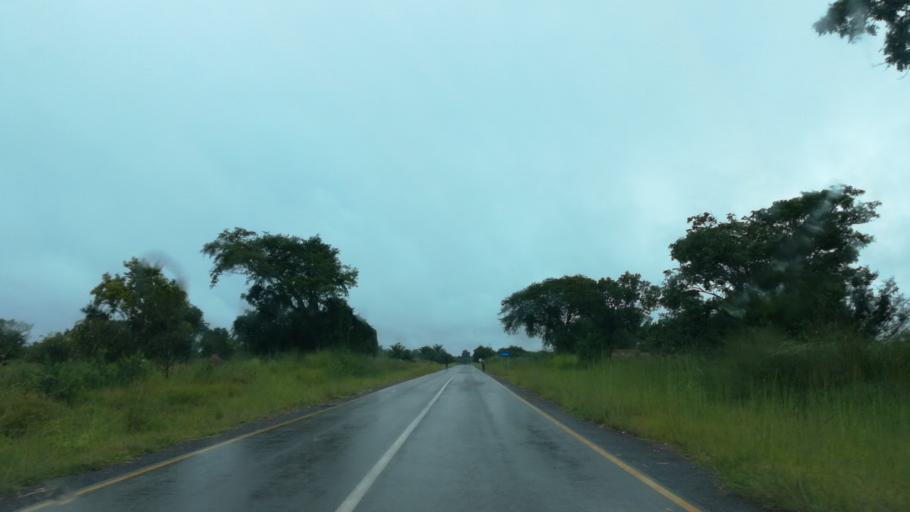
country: ZM
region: Luapula
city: Mwense
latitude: -10.8343
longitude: 28.2331
